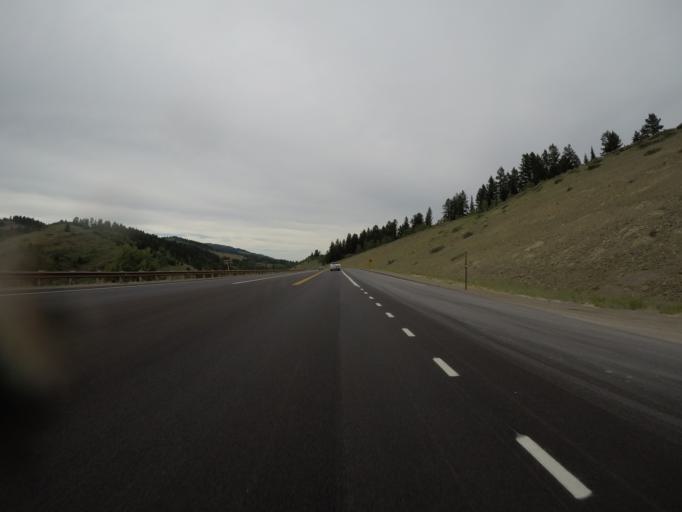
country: US
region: Wyoming
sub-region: Lincoln County
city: Afton
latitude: 42.5296
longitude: -110.8978
